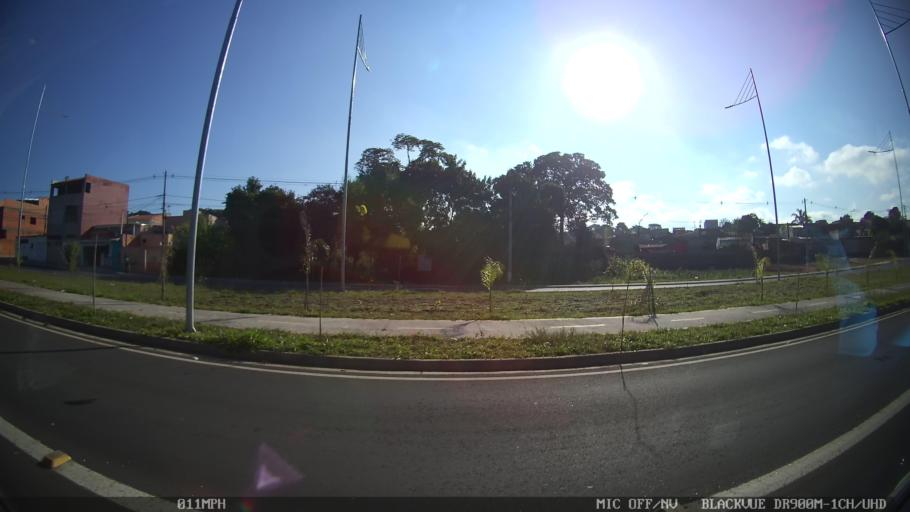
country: BR
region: Sao Paulo
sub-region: Hortolandia
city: Hortolandia
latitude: -22.8831
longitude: -47.1640
